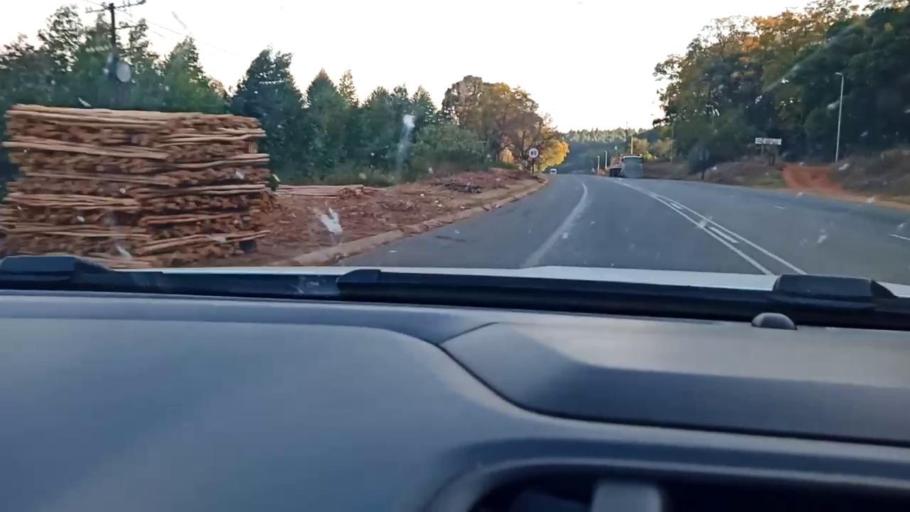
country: ZA
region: Limpopo
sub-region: Mopani District Municipality
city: Duiwelskloof
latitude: -23.7033
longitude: 30.1339
